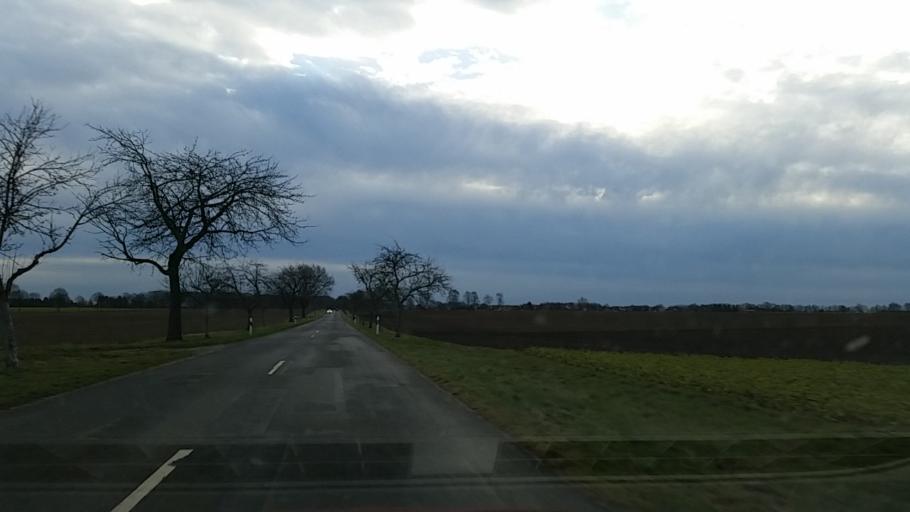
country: DE
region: Lower Saxony
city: Hankensbuttel
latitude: 52.7321
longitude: 10.5782
